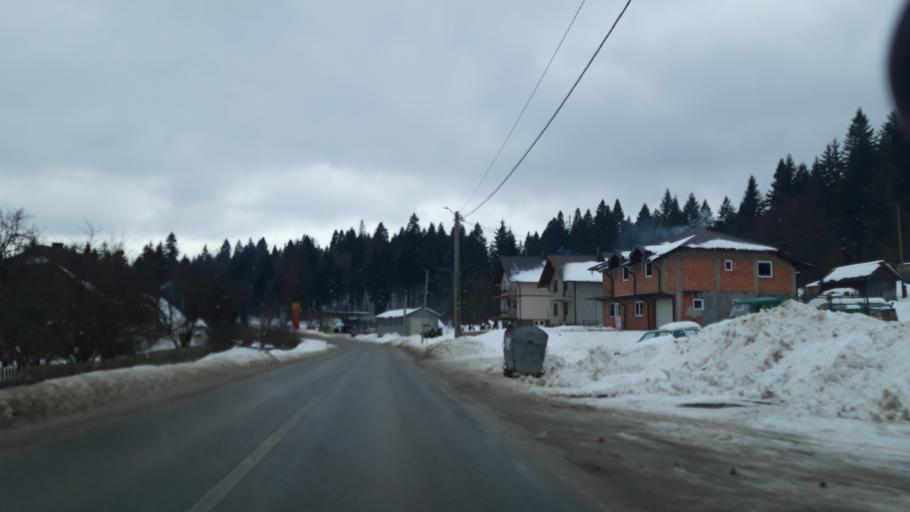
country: BA
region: Republika Srpska
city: Han Pijesak
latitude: 44.0703
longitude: 18.9462
